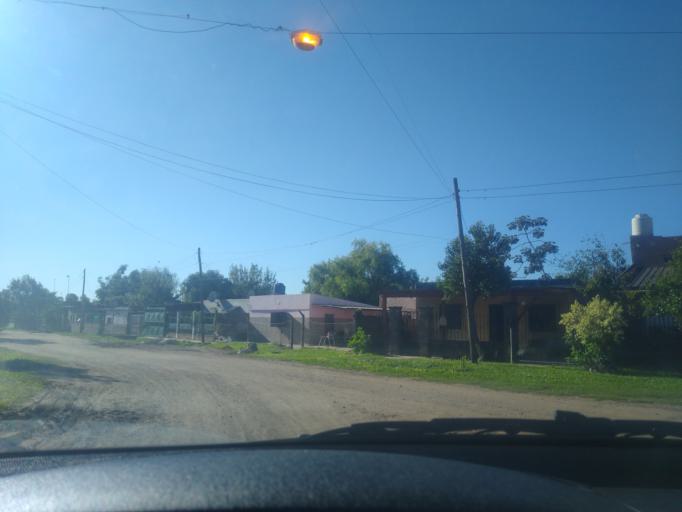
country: AR
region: Chaco
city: Puerto Vilelas
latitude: -27.5077
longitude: -58.9373
